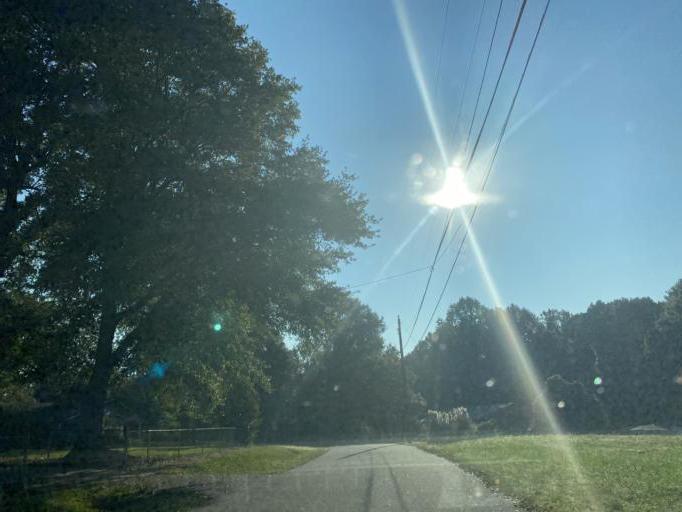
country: US
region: South Carolina
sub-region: Cherokee County
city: Gaffney
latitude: 35.0549
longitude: -81.6610
